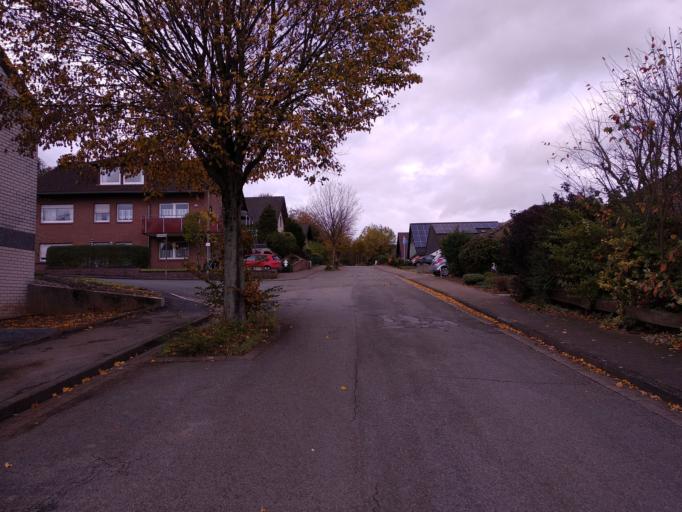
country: DE
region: North Rhine-Westphalia
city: Beverungen
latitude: 51.6704
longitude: 9.3680
